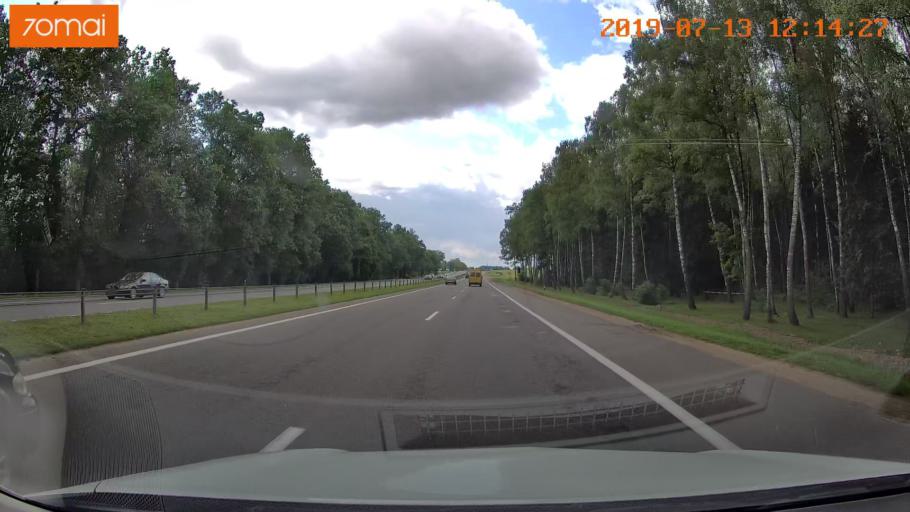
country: BY
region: Minsk
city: Samakhvalavichy
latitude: 53.7624
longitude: 27.5190
